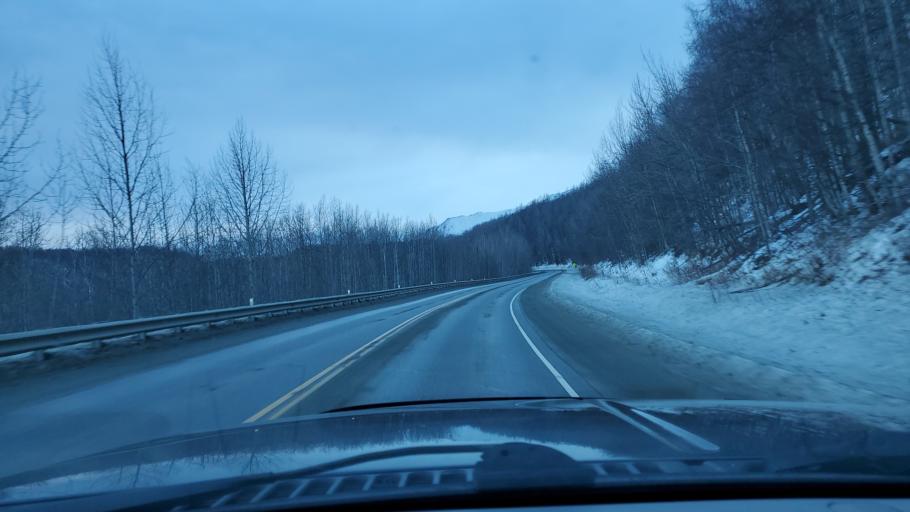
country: US
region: Alaska
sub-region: Matanuska-Susitna Borough
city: Lazy Mountain
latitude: 61.6791
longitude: -149.0299
